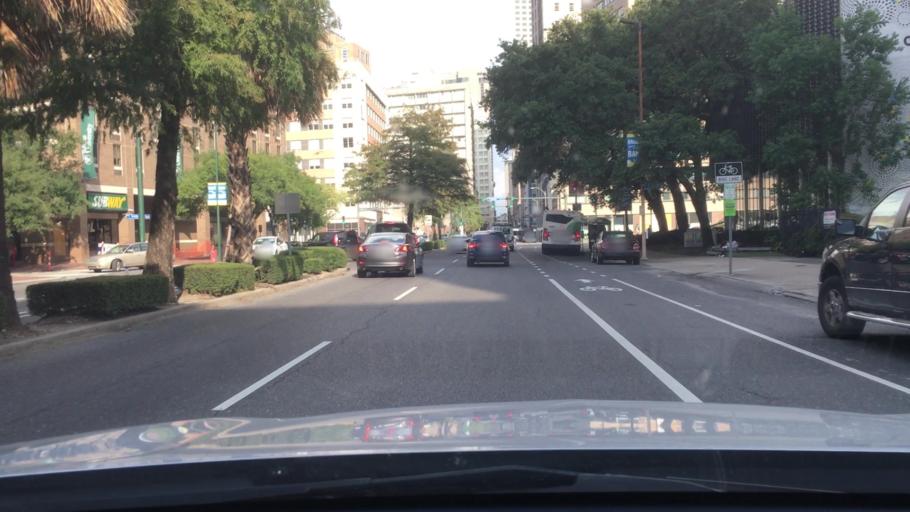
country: US
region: Louisiana
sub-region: Orleans Parish
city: New Orleans
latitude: 29.9551
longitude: -90.0759
